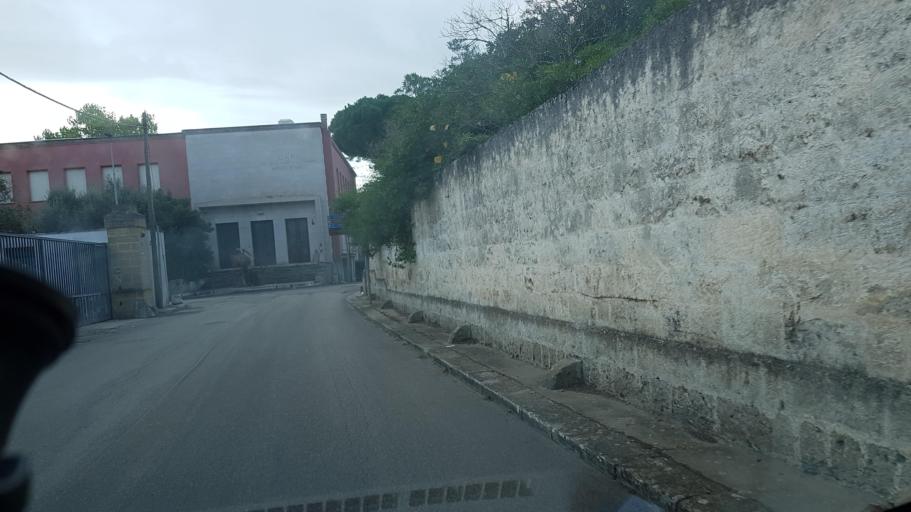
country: IT
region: Apulia
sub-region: Provincia di Brindisi
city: San Pietro Vernotico
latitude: 40.4883
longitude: 18.0016
